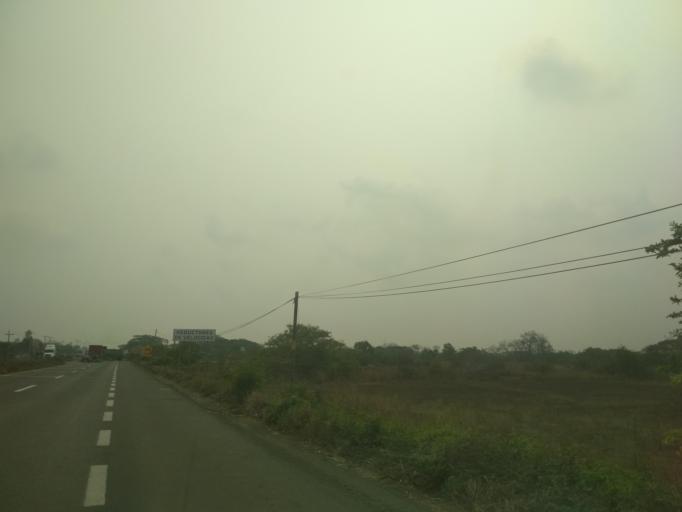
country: MX
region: Veracruz
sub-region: Veracruz
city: Delfino Victoria (Santa Fe)
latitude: 19.2080
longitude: -96.2627
